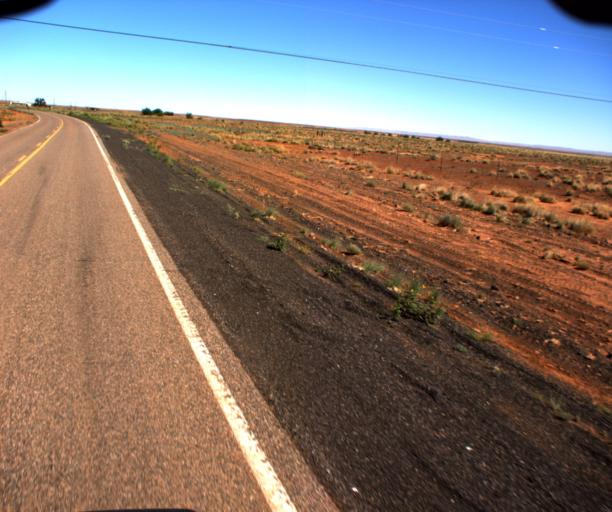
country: US
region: Arizona
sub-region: Coconino County
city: LeChee
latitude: 35.1516
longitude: -110.8989
